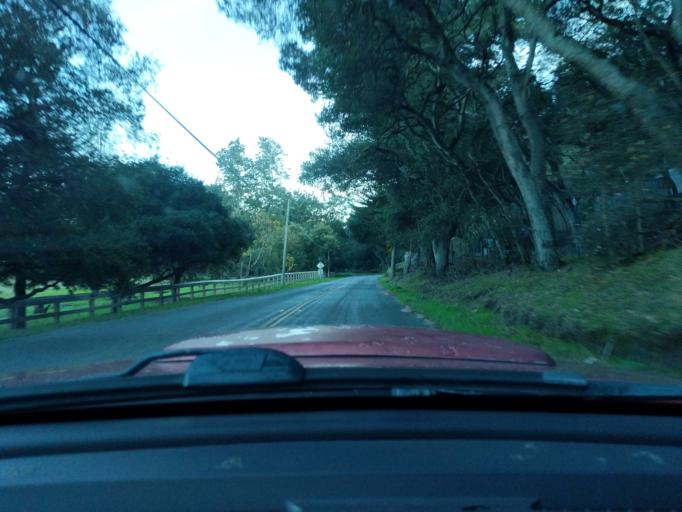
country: US
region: California
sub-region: San Benito County
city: Aromas
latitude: 36.8376
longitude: -121.6710
